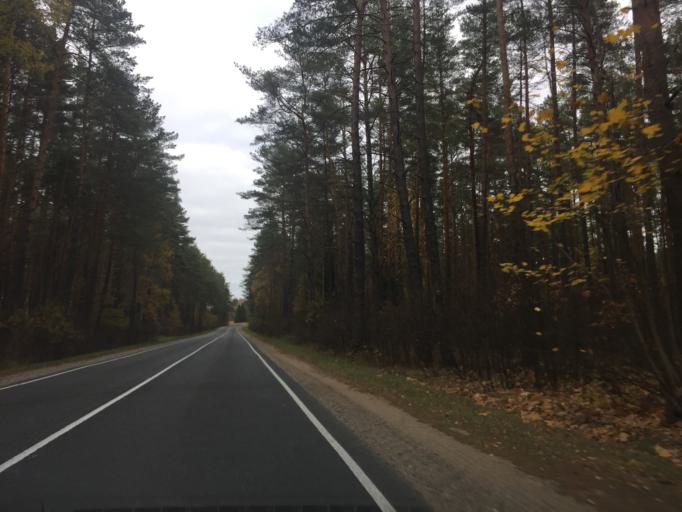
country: BY
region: Minsk
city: Svir
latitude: 54.8200
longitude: 26.1819
